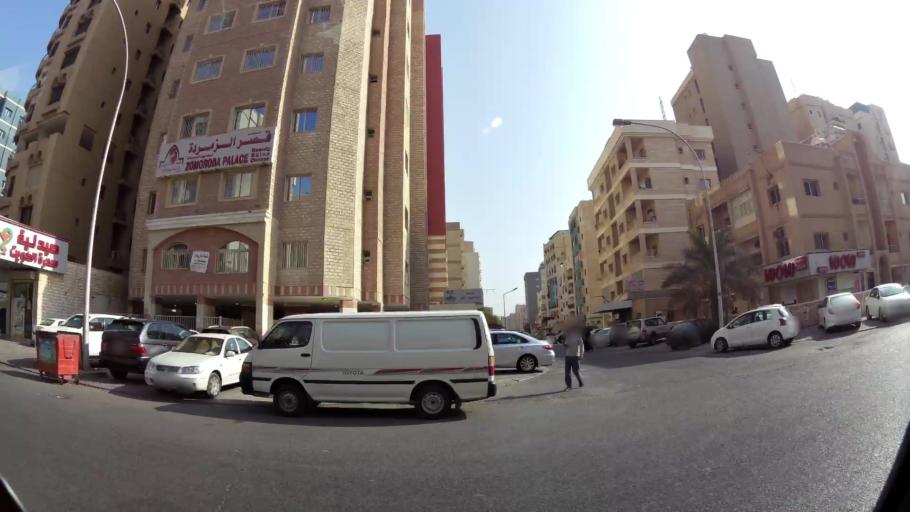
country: KW
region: Muhafazat Hawalli
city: Hawalli
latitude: 29.3283
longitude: 48.0121
